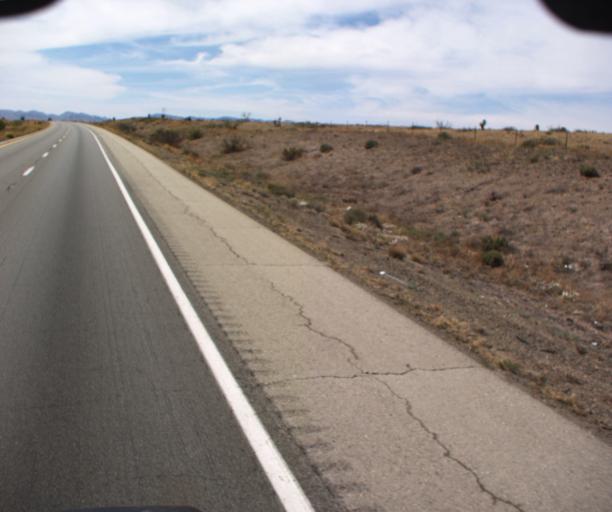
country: US
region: Arizona
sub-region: Cochise County
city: Willcox
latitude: 32.3496
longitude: -109.7386
